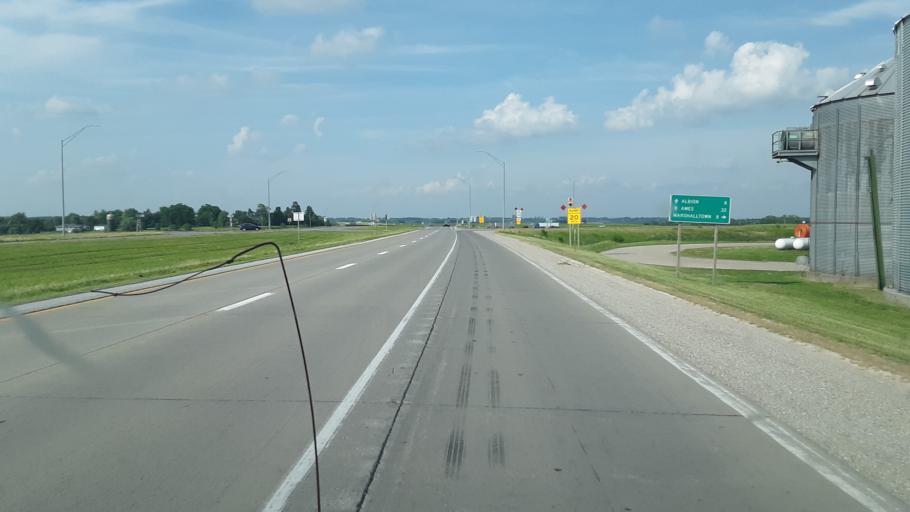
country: US
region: Iowa
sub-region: Marshall County
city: Marshalltown
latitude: 42.0055
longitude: -93.0230
